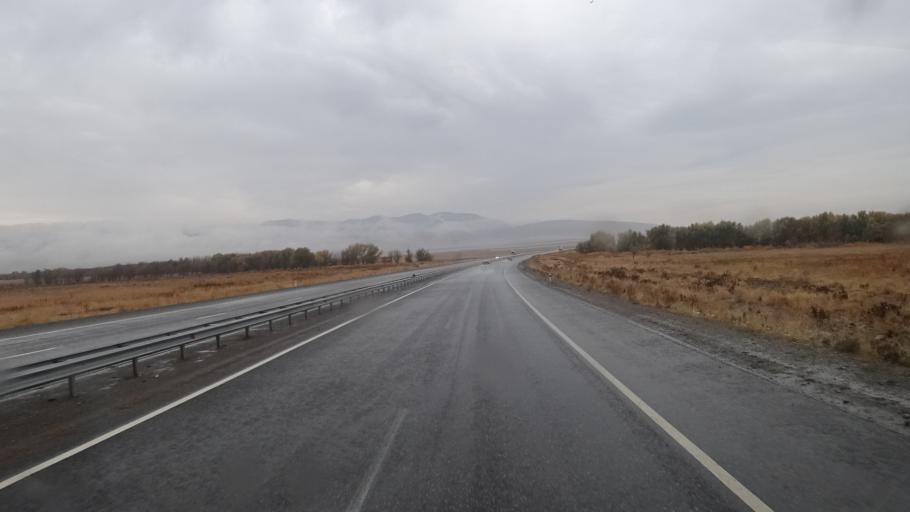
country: KZ
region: Ongtustik Qazaqstan
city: Kokterek
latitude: 42.5428
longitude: 70.2224
